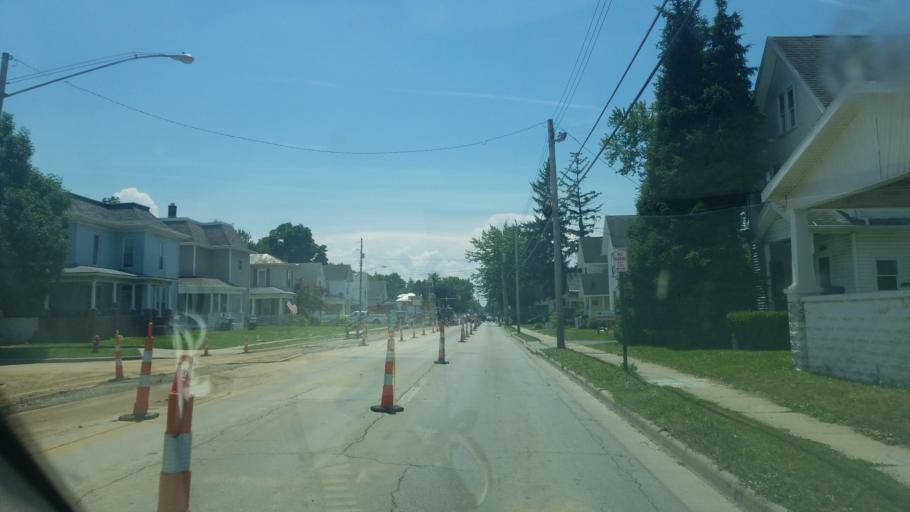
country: US
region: Ohio
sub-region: Hancock County
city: Findlay
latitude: 41.0360
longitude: -83.6413
